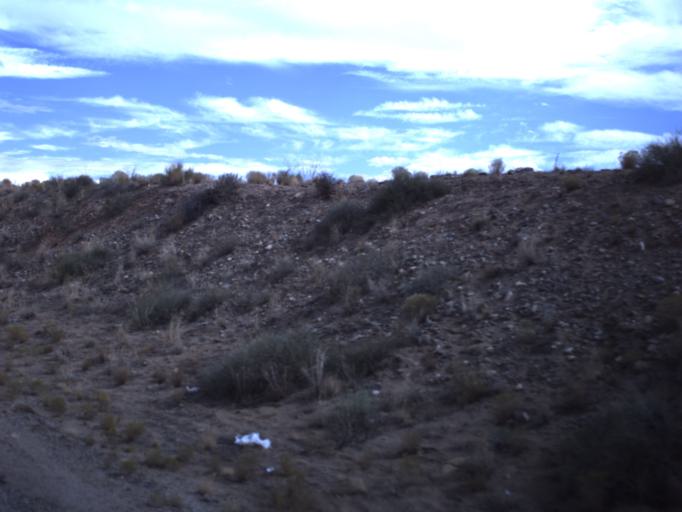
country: US
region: Utah
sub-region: San Juan County
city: Blanding
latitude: 37.2384
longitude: -109.2358
